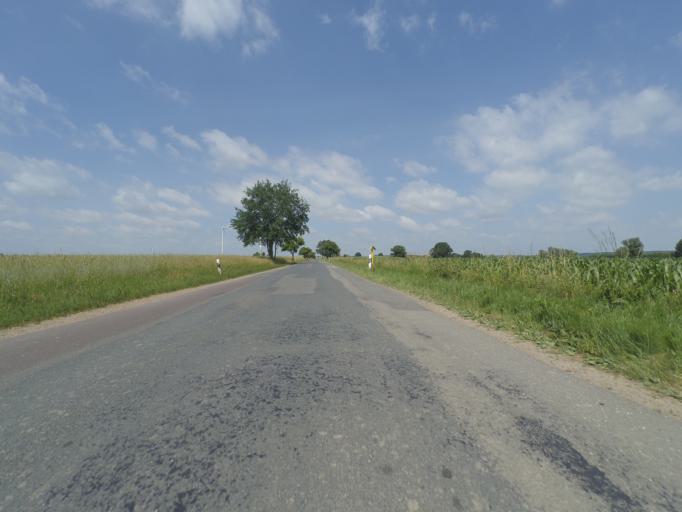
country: DE
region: Mecklenburg-Vorpommern
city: Lubz
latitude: 53.4433
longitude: 12.0111
